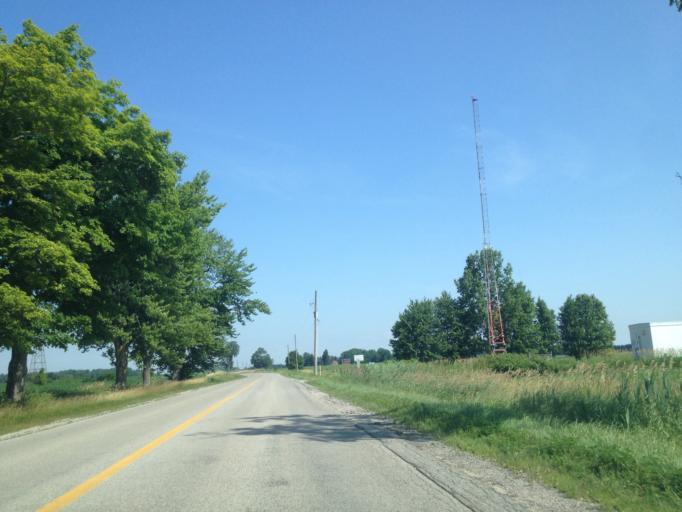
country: CA
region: Ontario
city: London
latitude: 43.0907
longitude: -81.2184
